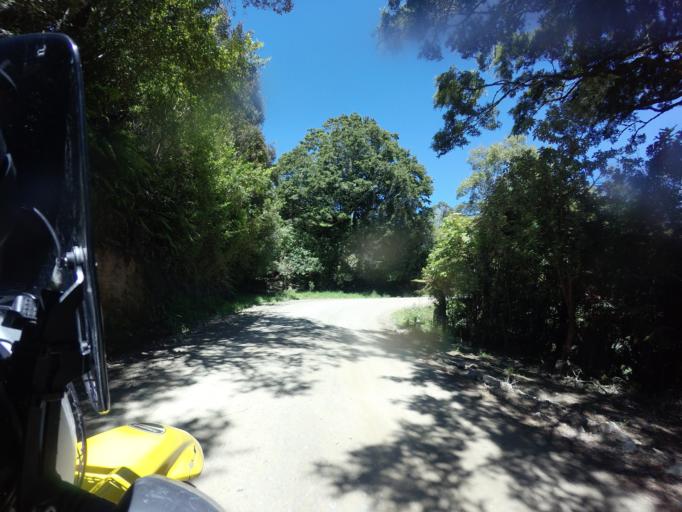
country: NZ
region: Bay of Plenty
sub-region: Opotiki District
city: Opotiki
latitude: -38.4089
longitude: 177.4455
